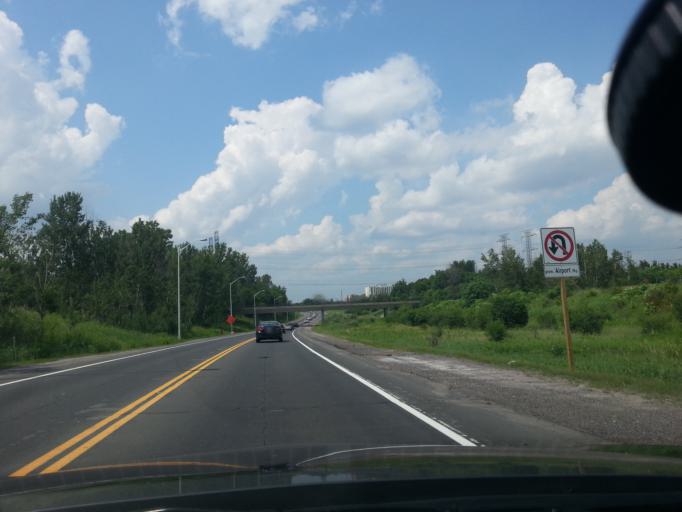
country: CA
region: Ontario
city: Ottawa
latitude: 45.3597
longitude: -75.6631
